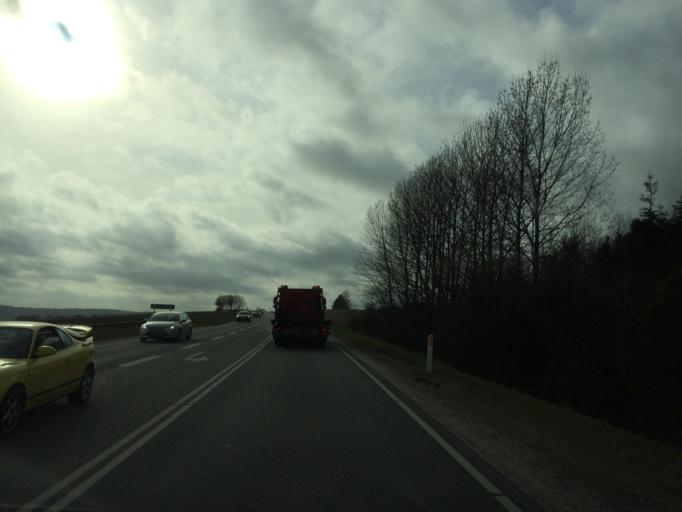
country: DK
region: Central Jutland
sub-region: Randers Kommune
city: Langa
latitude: 56.4798
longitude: 9.8936
